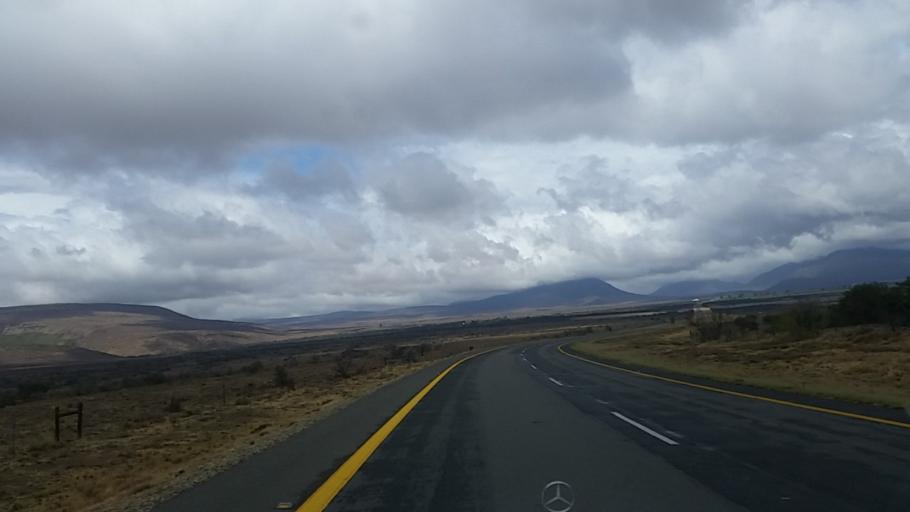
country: ZA
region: Eastern Cape
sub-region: Cacadu District Municipality
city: Graaff-Reinet
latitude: -32.1475
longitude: 24.5774
